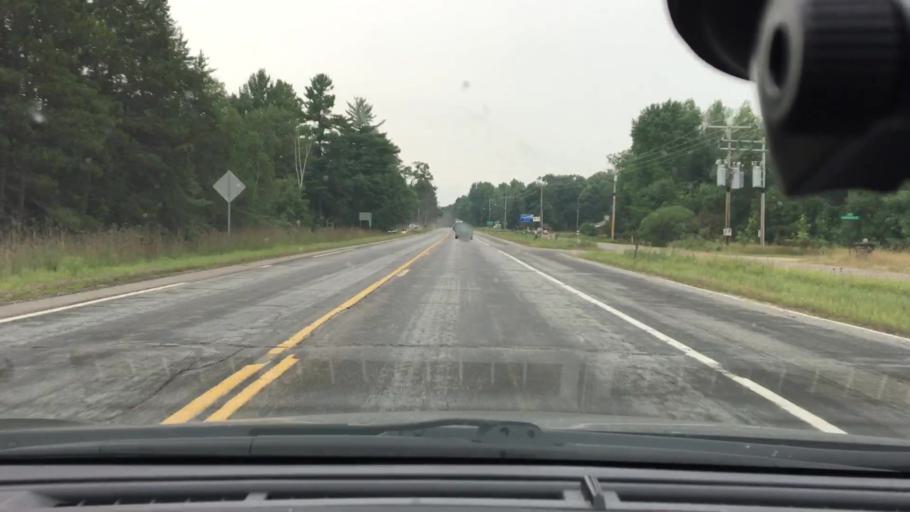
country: US
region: Minnesota
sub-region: Crow Wing County
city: Cross Lake
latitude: 46.7911
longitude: -93.9659
